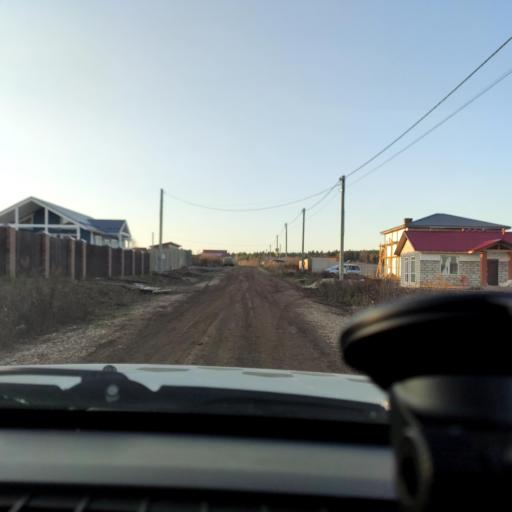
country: RU
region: Perm
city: Ferma
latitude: 57.9465
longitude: 56.3513
